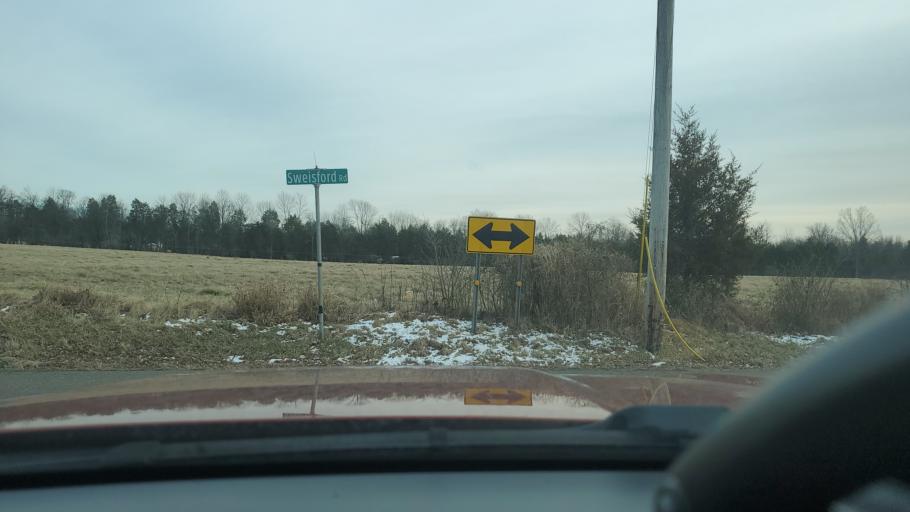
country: US
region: Pennsylvania
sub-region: Montgomery County
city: Woxall
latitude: 40.3157
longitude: -75.5088
